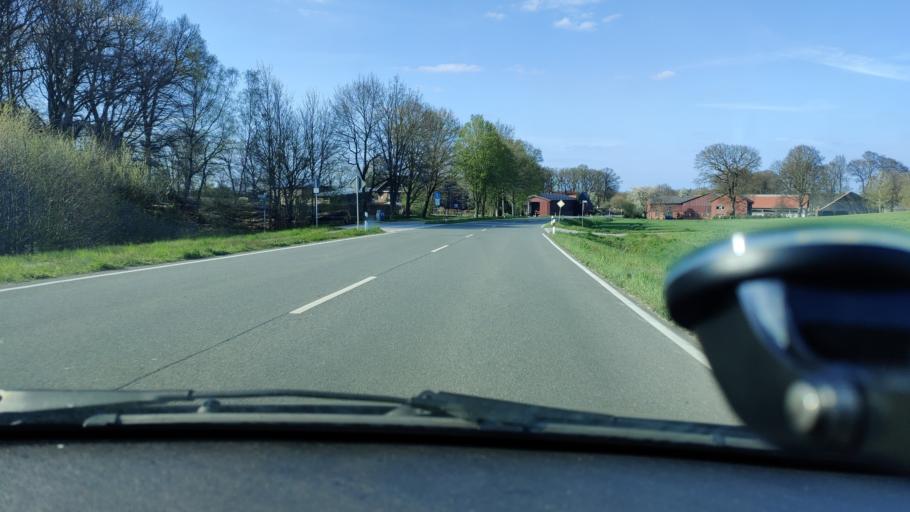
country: DE
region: North Rhine-Westphalia
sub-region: Regierungsbezirk Munster
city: Klein Reken
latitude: 51.8440
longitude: 7.0535
